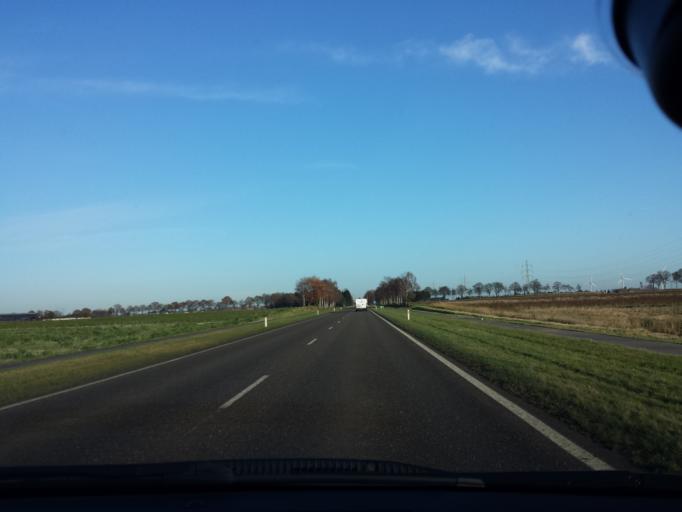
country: NL
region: Limburg
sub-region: Gemeente Echt-Susteren
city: Koningsbosch
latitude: 51.0384
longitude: 5.9466
